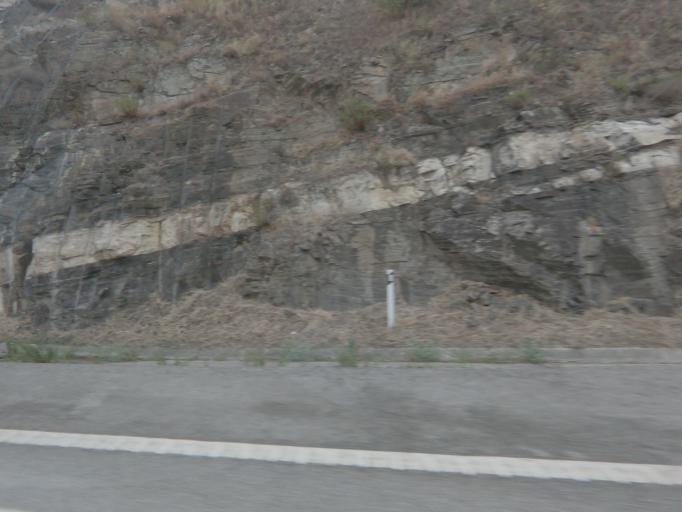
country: PT
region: Vila Real
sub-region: Peso da Regua
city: Peso da Regua
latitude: 41.1347
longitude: -7.7719
